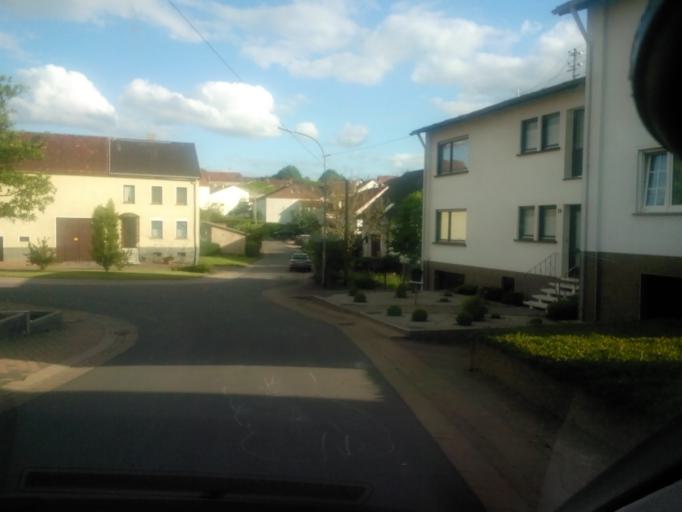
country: DE
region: Saarland
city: Merzig
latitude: 49.3780
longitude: 6.5921
